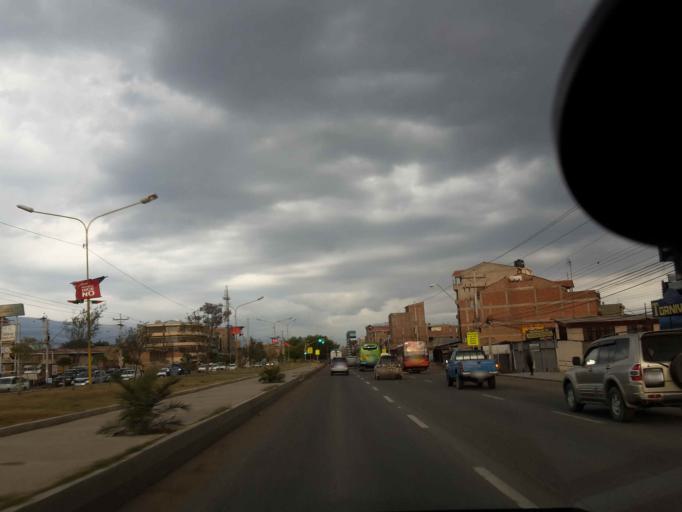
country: BO
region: Cochabamba
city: Sipe Sipe
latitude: -17.3945
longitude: -66.2882
